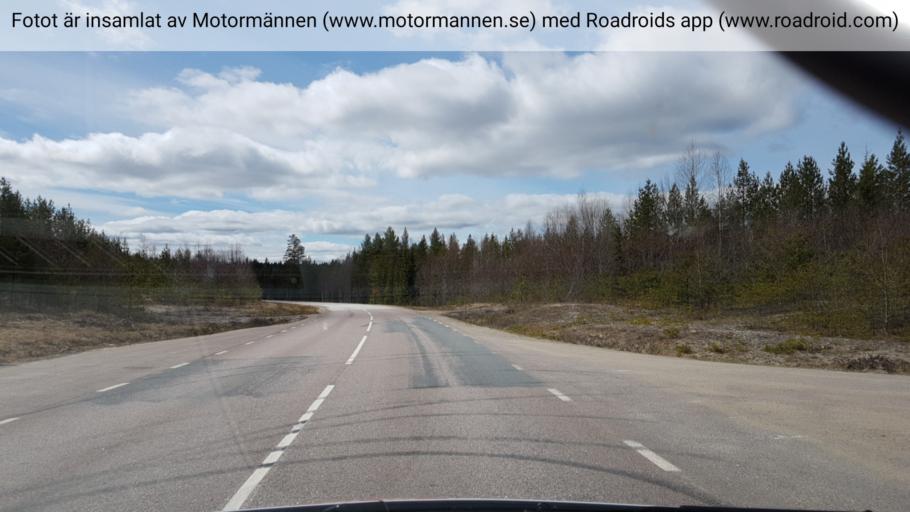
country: SE
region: Vaesternorrland
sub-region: OErnskoeldsviks Kommun
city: Ornskoldsvik
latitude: 63.6133
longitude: 18.6403
